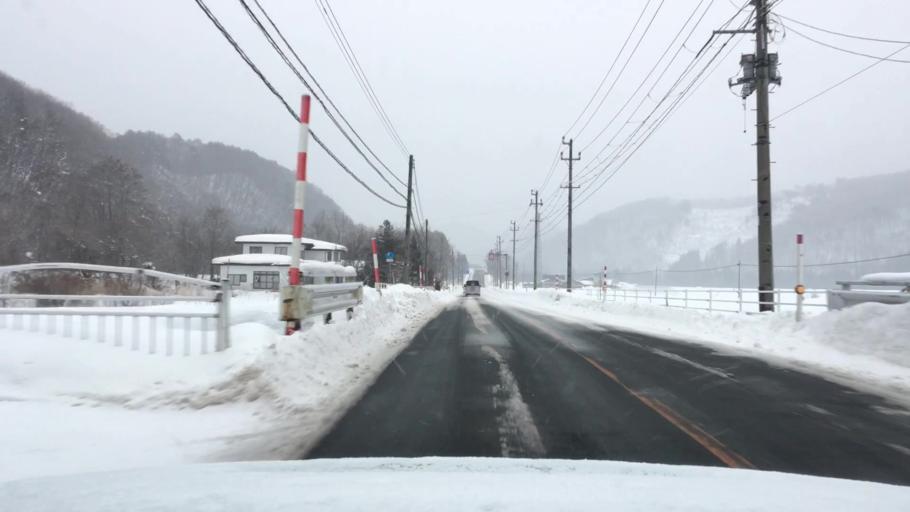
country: JP
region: Akita
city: Hanawa
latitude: 40.0579
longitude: 141.0110
